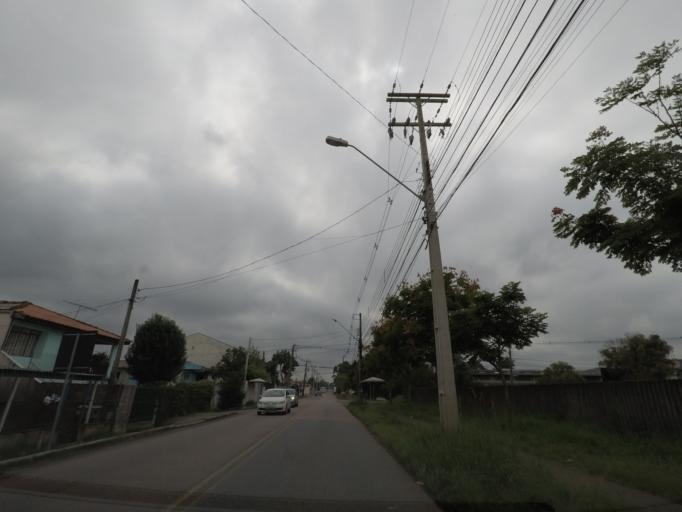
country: BR
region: Parana
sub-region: Curitiba
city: Curitiba
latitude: -25.5000
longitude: -49.3350
